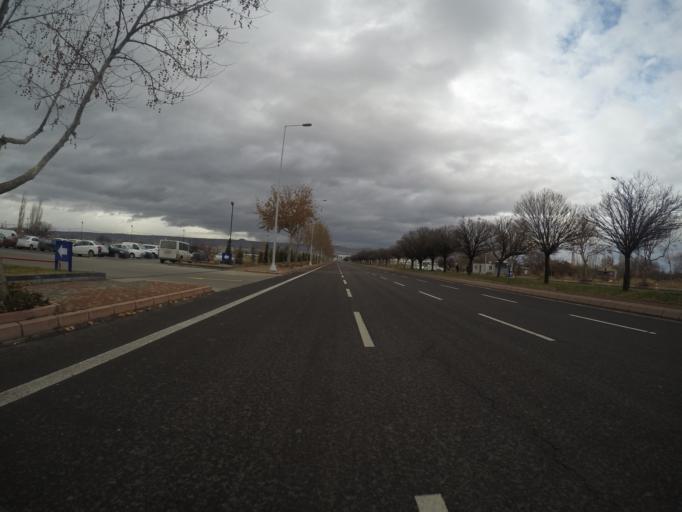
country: TR
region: Kayseri
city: Kayseri
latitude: 38.7594
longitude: 35.4823
